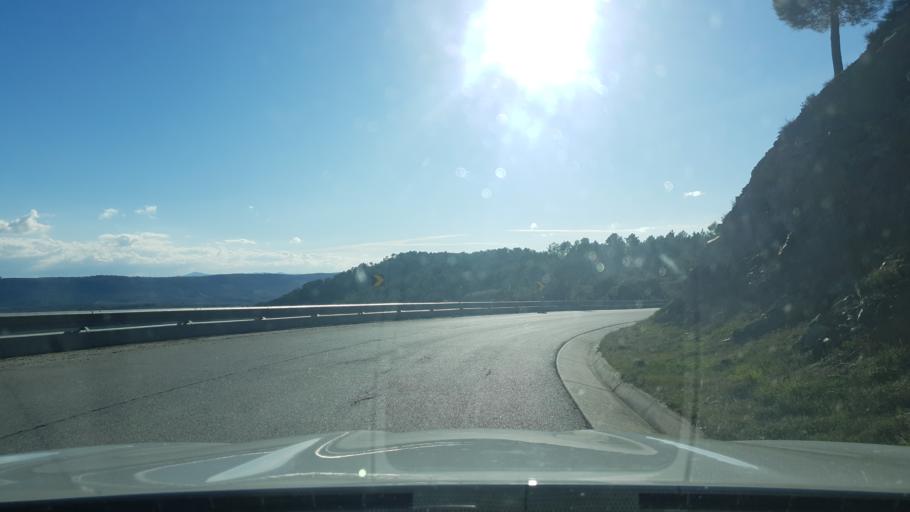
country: PT
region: Braganca
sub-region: Freixo de Espada A Cinta
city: Freixo de Espada a Cinta
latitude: 41.1116
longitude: -6.8211
